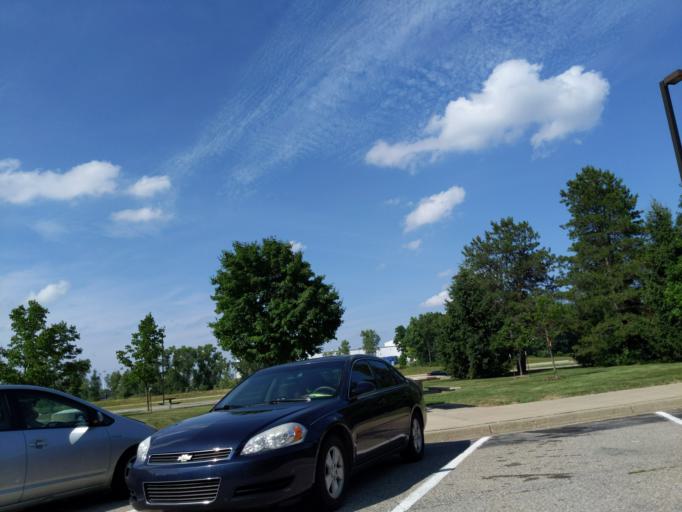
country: US
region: Michigan
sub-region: Livingston County
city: Howell
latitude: 42.6040
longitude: -83.9573
